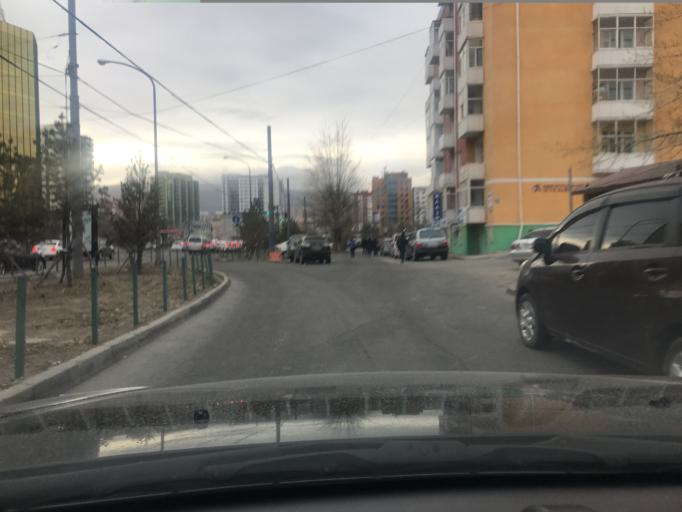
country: MN
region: Ulaanbaatar
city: Ulaanbaatar
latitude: 47.9203
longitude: 106.9427
